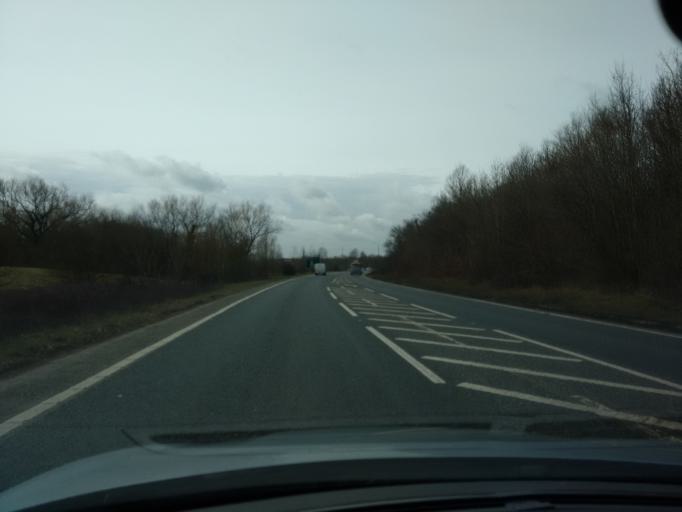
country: GB
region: England
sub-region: Worcestershire
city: Evesham
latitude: 52.0780
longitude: -1.9332
